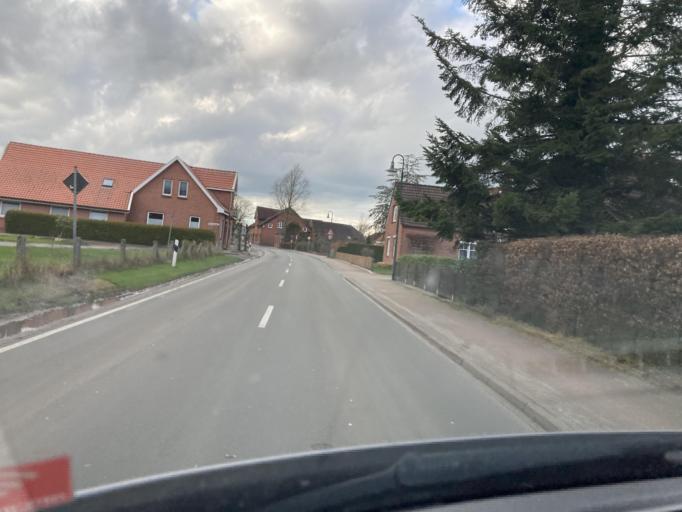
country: DE
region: Lower Saxony
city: Ostrhauderfehn
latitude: 53.1698
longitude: 7.5706
